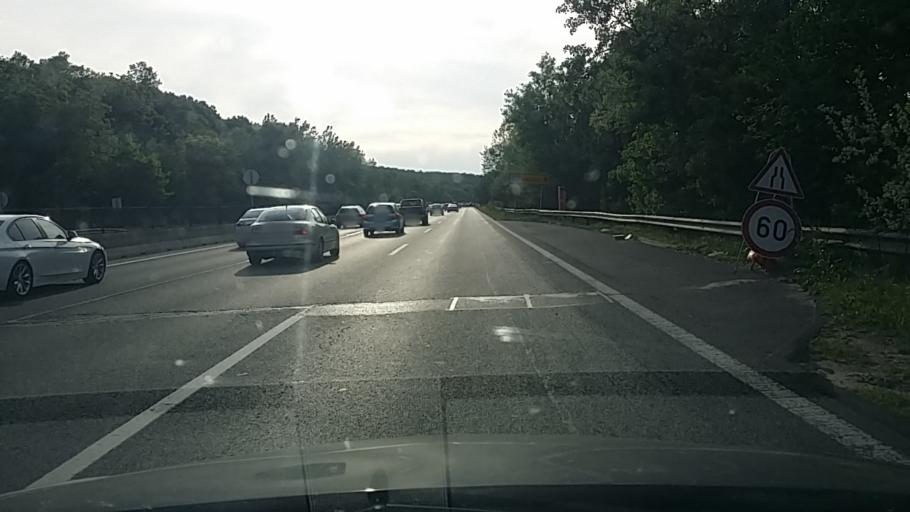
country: HU
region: Pest
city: Godollo
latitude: 47.6127
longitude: 19.3919
